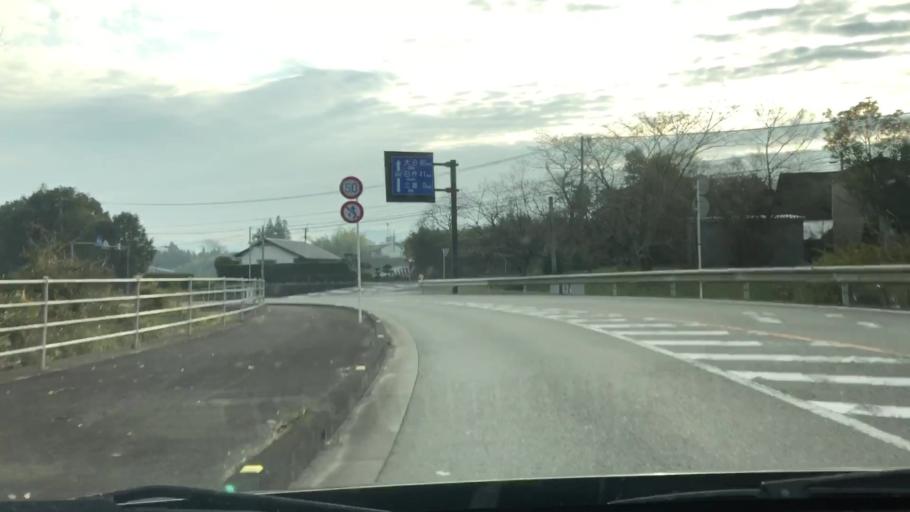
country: JP
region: Oita
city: Takedamachi
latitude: 32.9687
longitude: 131.5101
